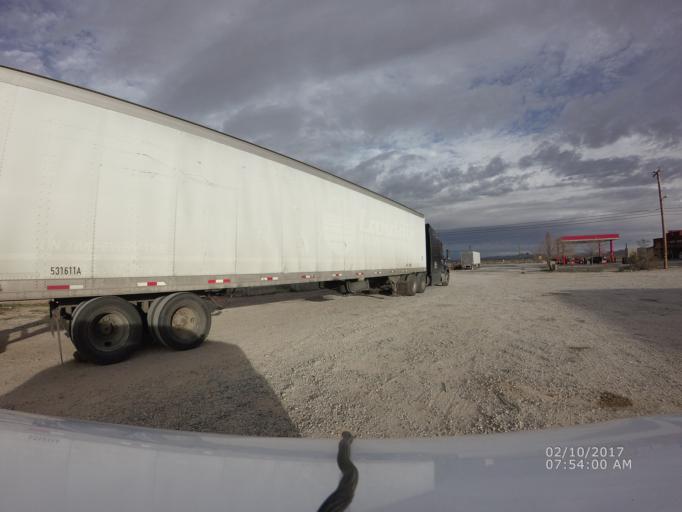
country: US
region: California
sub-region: Los Angeles County
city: Littlerock
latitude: 34.5054
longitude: -117.8980
